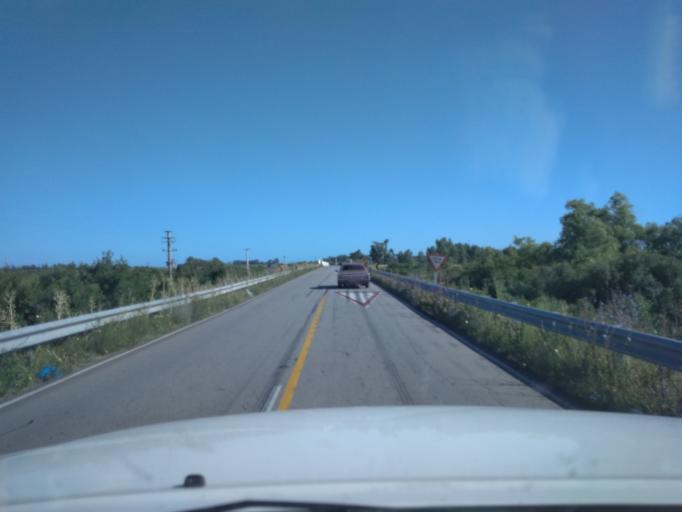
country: UY
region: Canelones
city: San Ramon
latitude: -34.3249
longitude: -55.9613
